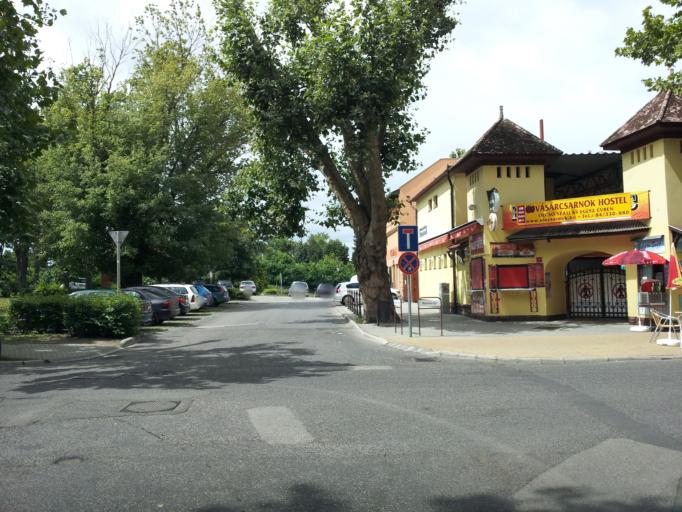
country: HU
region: Somogy
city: Siofok
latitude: 46.9074
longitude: 18.0484
